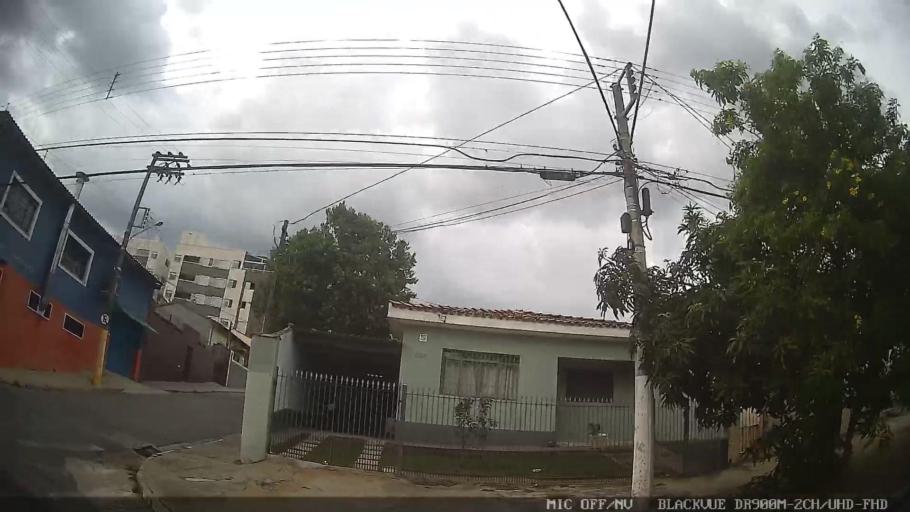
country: BR
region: Sao Paulo
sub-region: Atibaia
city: Atibaia
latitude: -23.1255
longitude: -46.5661
